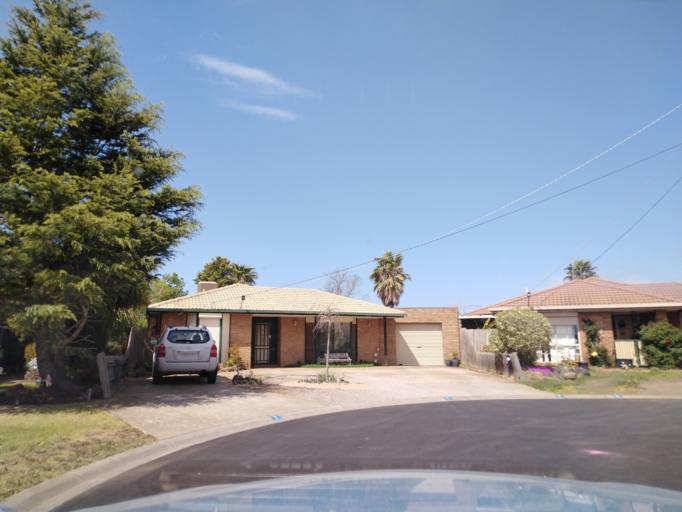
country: AU
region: Victoria
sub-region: Wyndham
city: Hoppers Crossing
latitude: -37.8595
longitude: 144.7070
